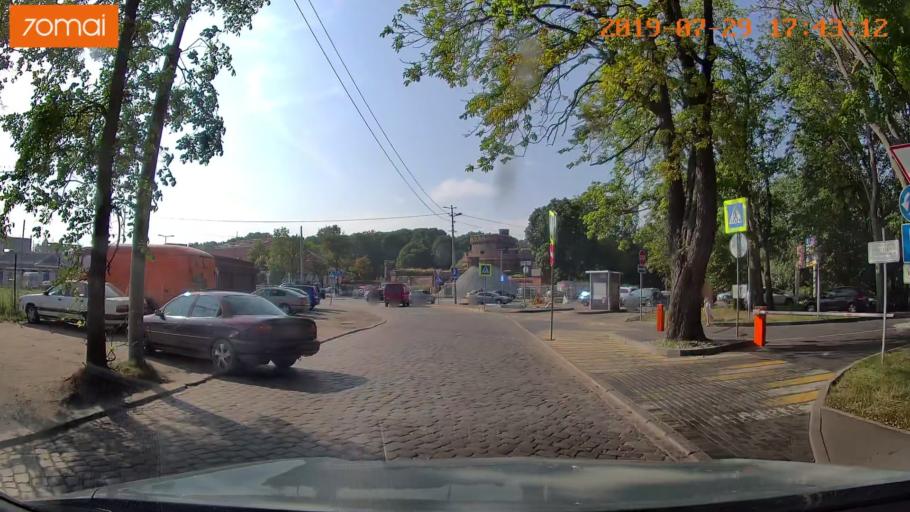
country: RU
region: Kaliningrad
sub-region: Gorod Kaliningrad
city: Kaliningrad
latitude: 54.7219
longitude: 20.5172
